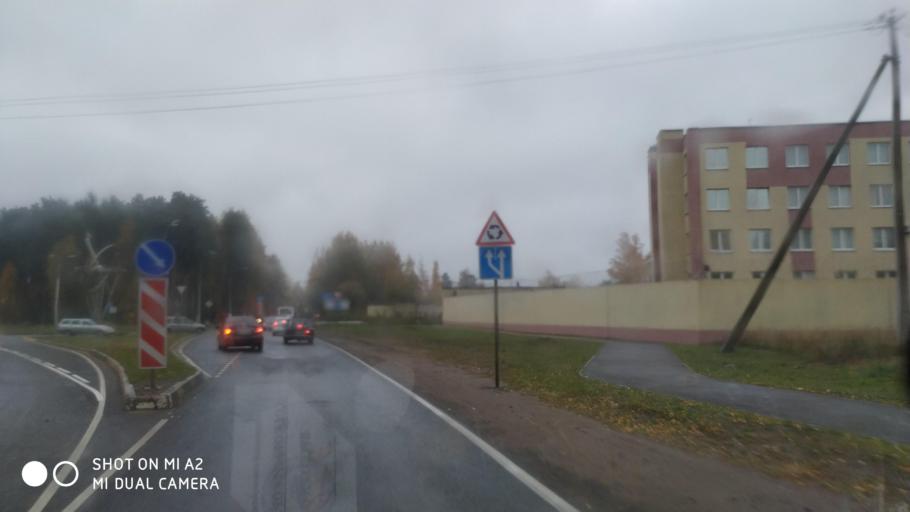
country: RU
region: Leningrad
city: Sosnovyy Bor
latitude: 59.8938
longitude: 29.1120
